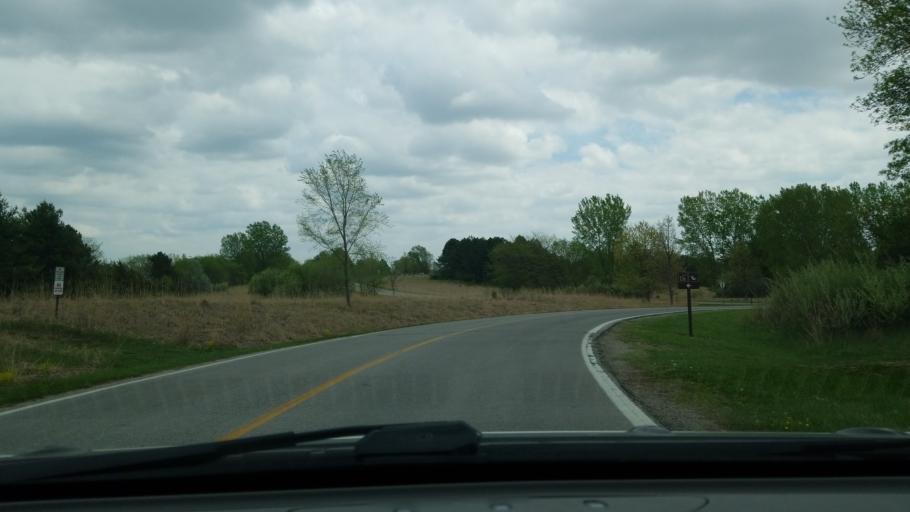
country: US
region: Nebraska
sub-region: Sarpy County
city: Chalco
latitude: 41.1656
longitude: -96.1642
